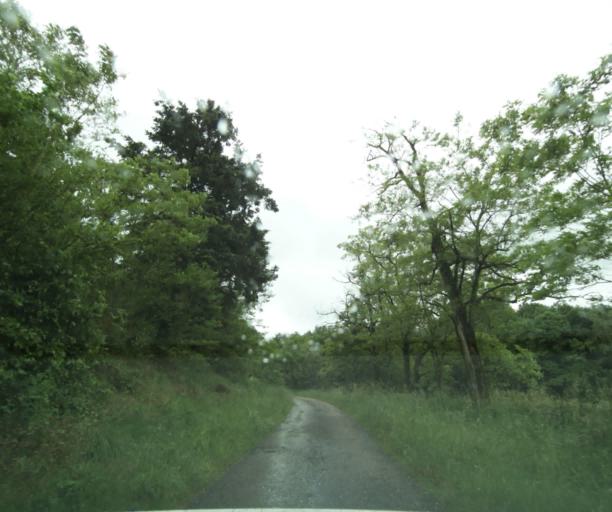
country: FR
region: Bourgogne
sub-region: Departement de Saone-et-Loire
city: Matour
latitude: 46.4526
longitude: 4.4649
